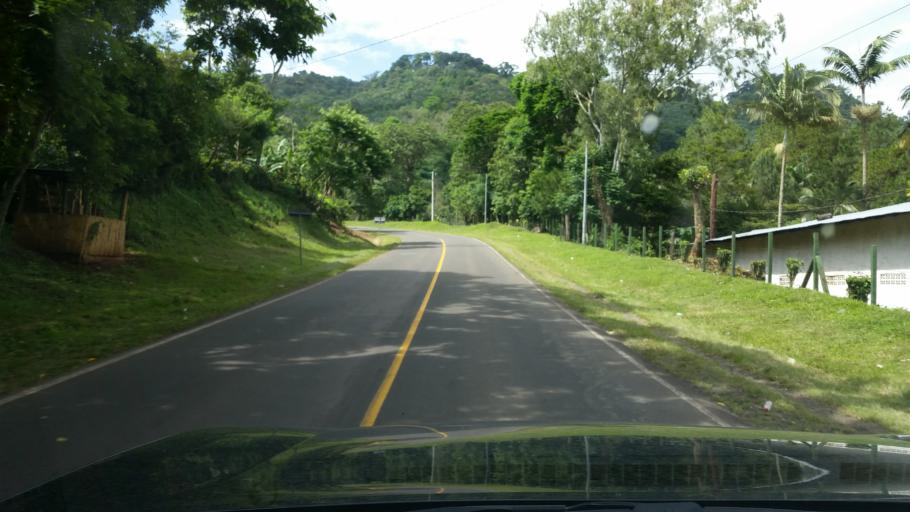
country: NI
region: Matagalpa
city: San Ramon
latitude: 12.9604
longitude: -85.8695
